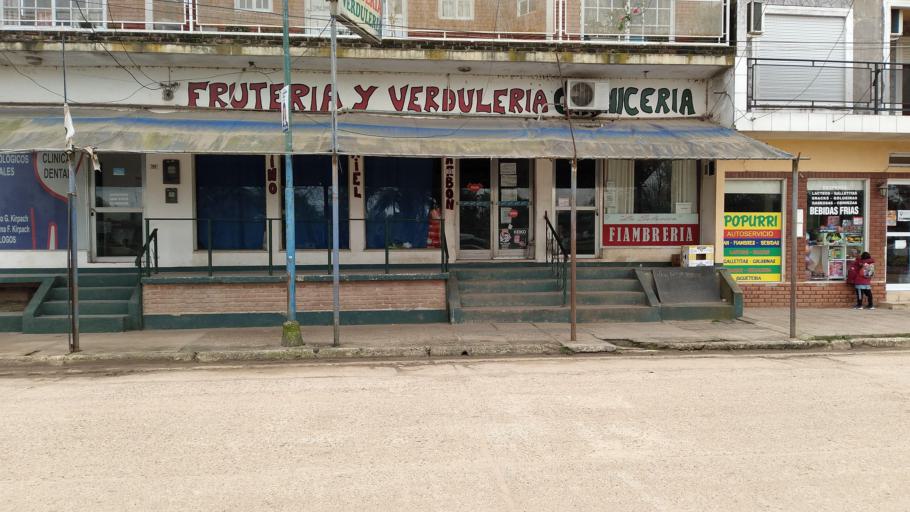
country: AR
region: Entre Rios
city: Villa Paranacito
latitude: -33.7163
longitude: -58.6607
